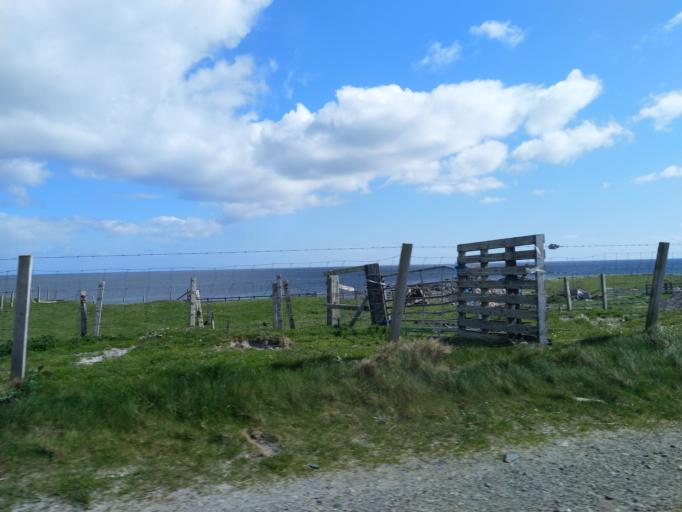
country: GB
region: Scotland
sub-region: Eilean Siar
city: Barra
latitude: 56.4821
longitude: -6.8837
